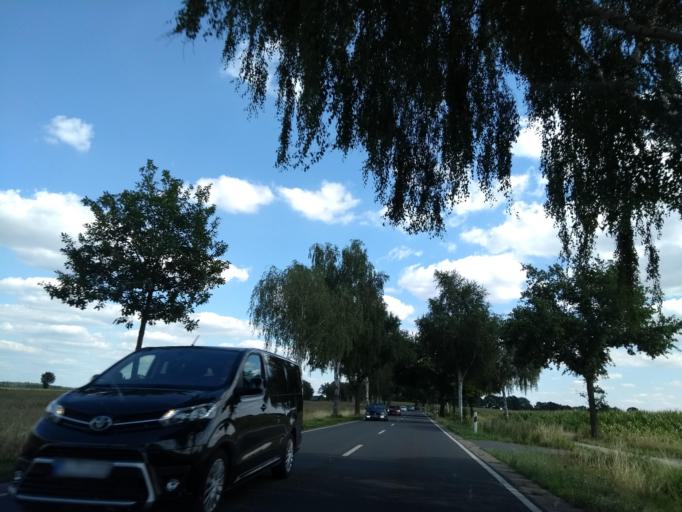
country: DE
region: Lower Saxony
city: Wunstorf
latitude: 52.4535
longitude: 9.4065
